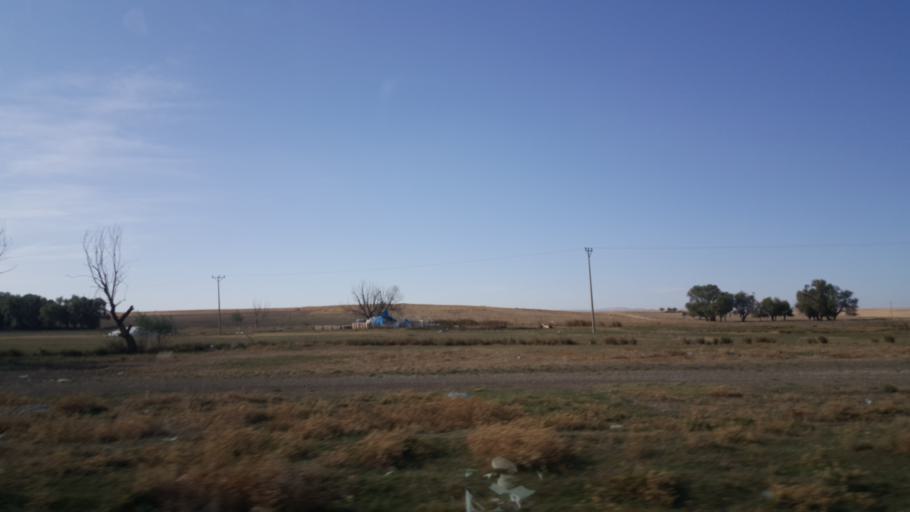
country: TR
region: Ankara
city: Yenice
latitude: 39.3638
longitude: 32.8099
